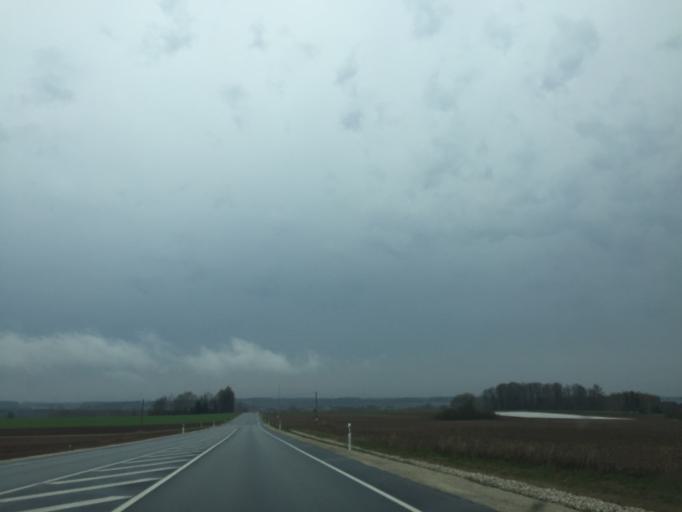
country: EE
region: Tartu
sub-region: UElenurme vald
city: Ulenurme
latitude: 58.2403
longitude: 26.6876
